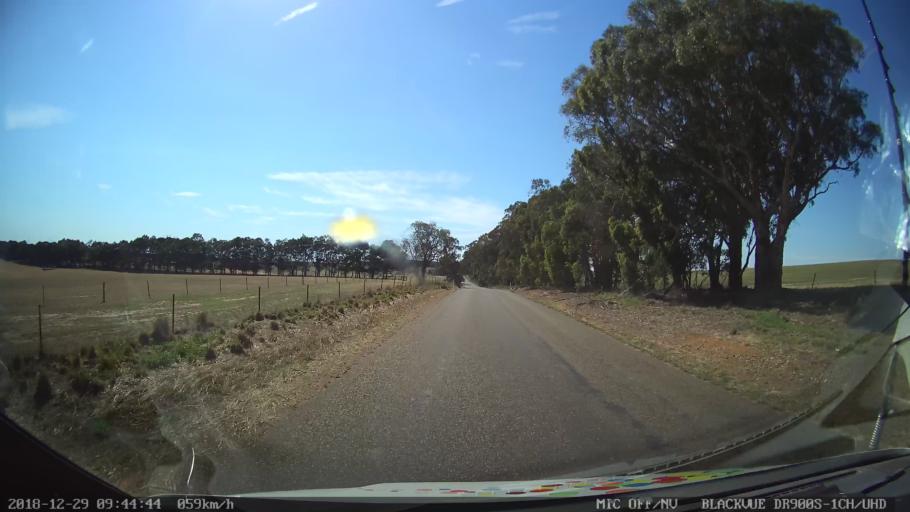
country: AU
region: New South Wales
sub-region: Upper Lachlan Shire
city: Crookwell
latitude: -34.6915
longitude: 149.4281
